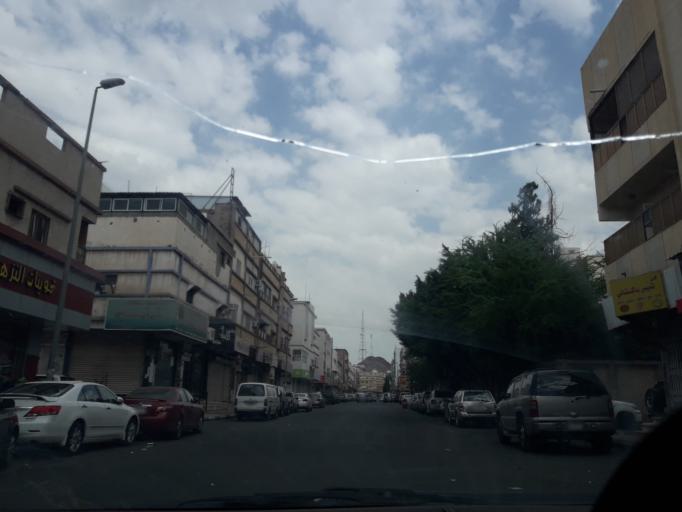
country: SA
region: Makkah
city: Ta'if
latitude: 21.2587
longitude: 40.4144
